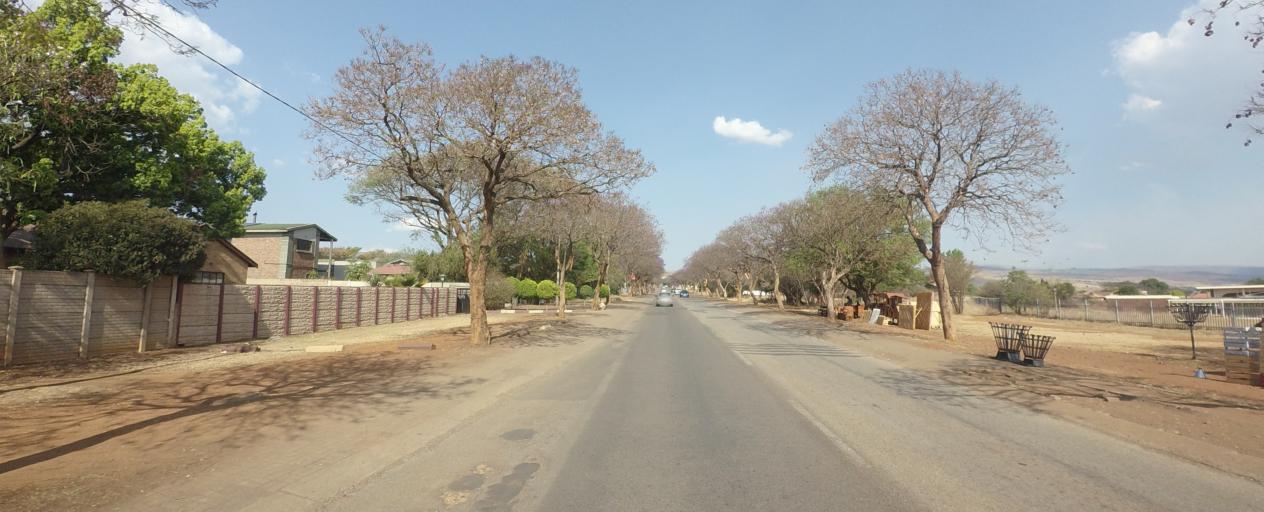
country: ZA
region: Mpumalanga
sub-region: Ehlanzeni District
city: Lydenburg
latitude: -25.1000
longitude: 30.4669
